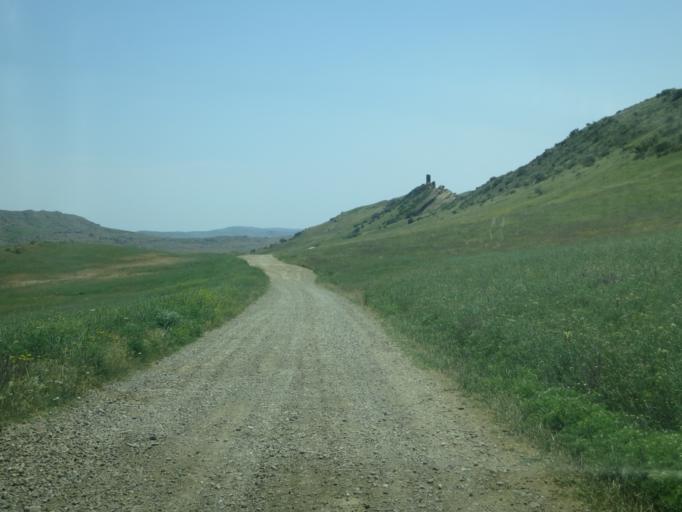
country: AZ
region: Agstafa
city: Saloglu
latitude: 41.4619
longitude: 45.3419
